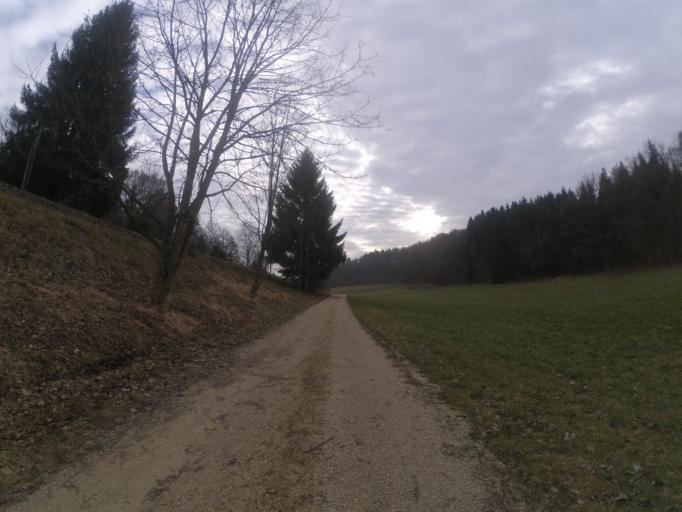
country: DE
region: Baden-Wuerttemberg
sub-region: Tuebingen Region
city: Mehrstetten
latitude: 48.3659
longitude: 9.5390
